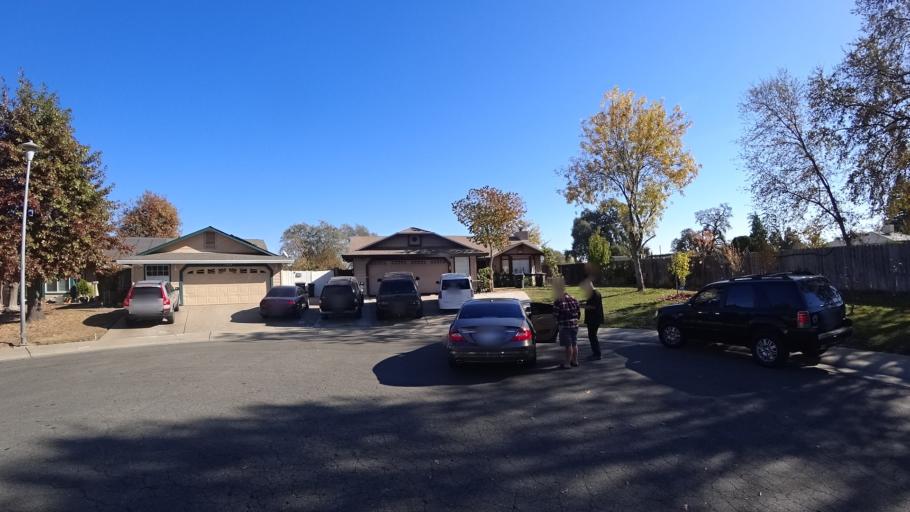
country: US
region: California
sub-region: Sacramento County
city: Antelope
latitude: 38.7220
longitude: -121.3065
